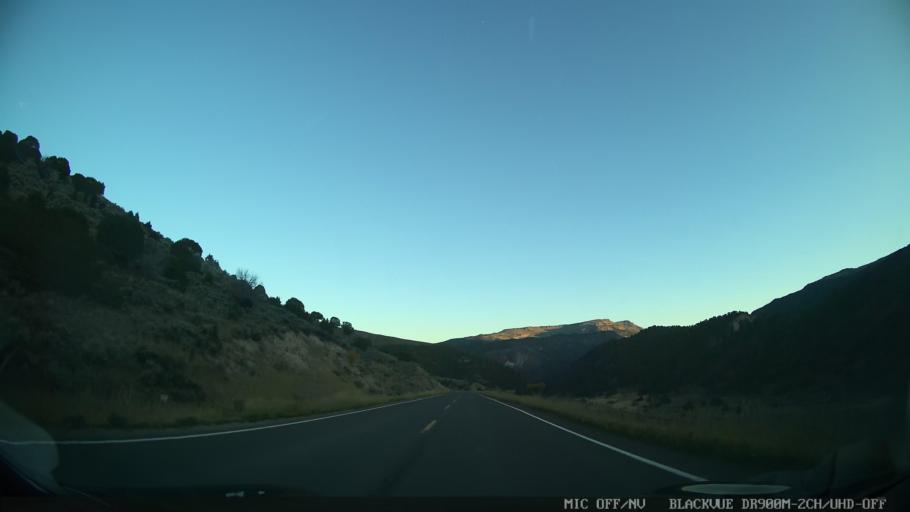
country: US
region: Colorado
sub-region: Eagle County
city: Edwards
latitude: 39.8393
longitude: -106.6406
